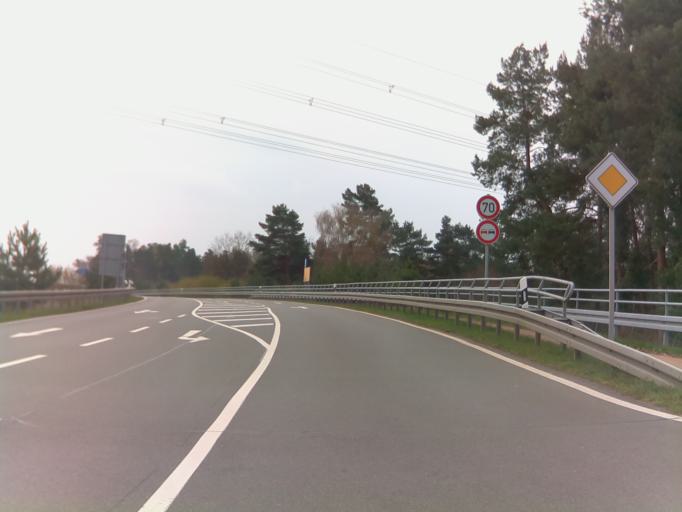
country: DE
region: Saxony-Anhalt
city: Coswig
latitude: 51.9636
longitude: 12.4639
